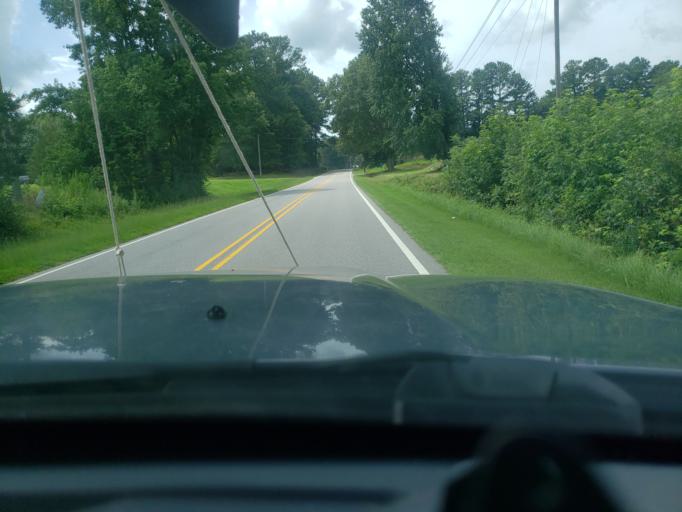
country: US
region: North Carolina
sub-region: Wake County
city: Rolesville
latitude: 35.8818
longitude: -78.3866
